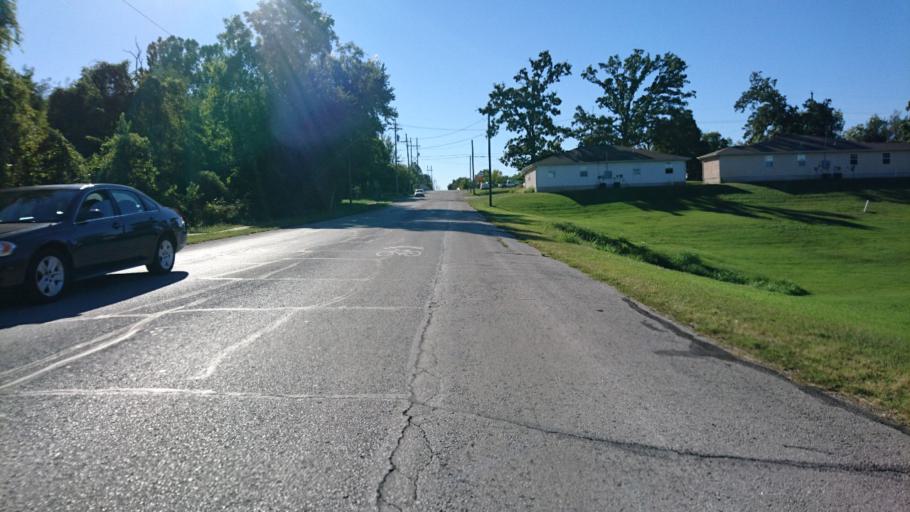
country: US
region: Missouri
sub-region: Jasper County
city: Carthage
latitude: 37.1765
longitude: -94.3309
